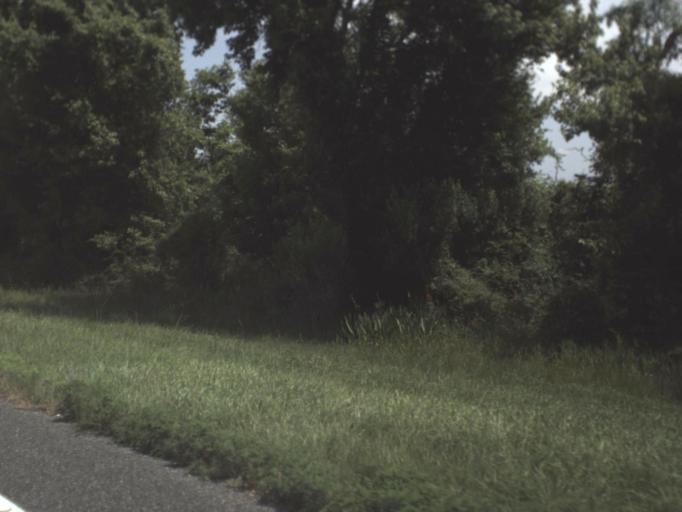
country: US
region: Florida
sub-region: Taylor County
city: Steinhatchee
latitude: 29.8290
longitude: -83.3598
